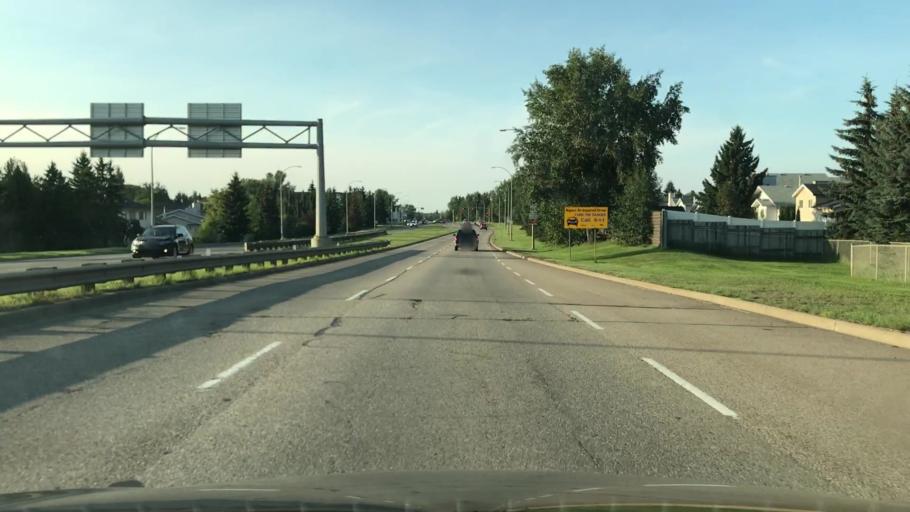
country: CA
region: Alberta
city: Beaumont
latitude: 53.4393
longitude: -113.4183
